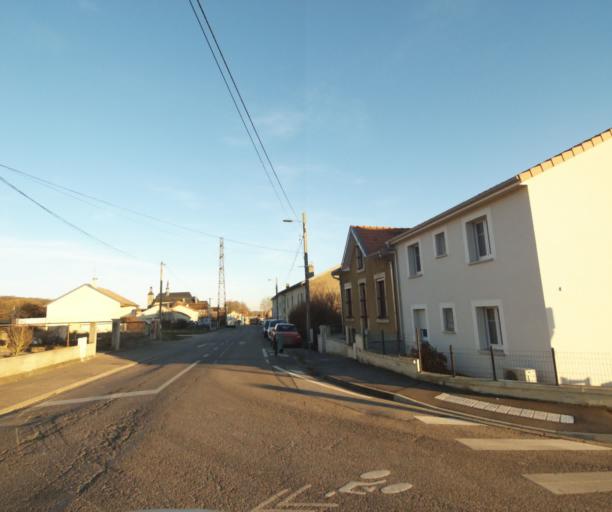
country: FR
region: Lorraine
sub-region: Departement de Meurthe-et-Moselle
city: Laneuveville-devant-Nancy
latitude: 48.6648
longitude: 6.2392
